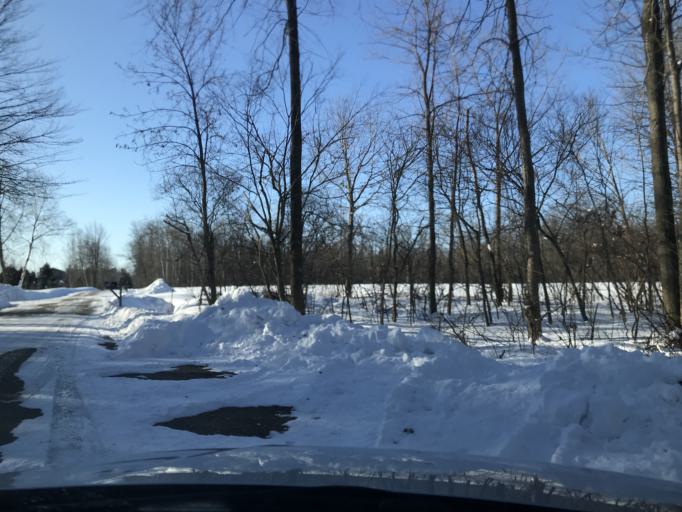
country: US
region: Wisconsin
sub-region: Oconto County
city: Oconto
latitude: 44.9574
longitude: -87.9769
